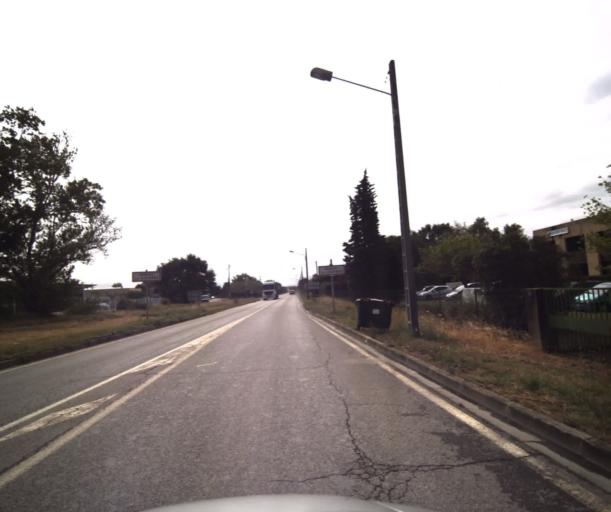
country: FR
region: Midi-Pyrenees
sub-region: Departement de la Haute-Garonne
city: Pinsaguel
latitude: 43.5285
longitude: 1.3736
